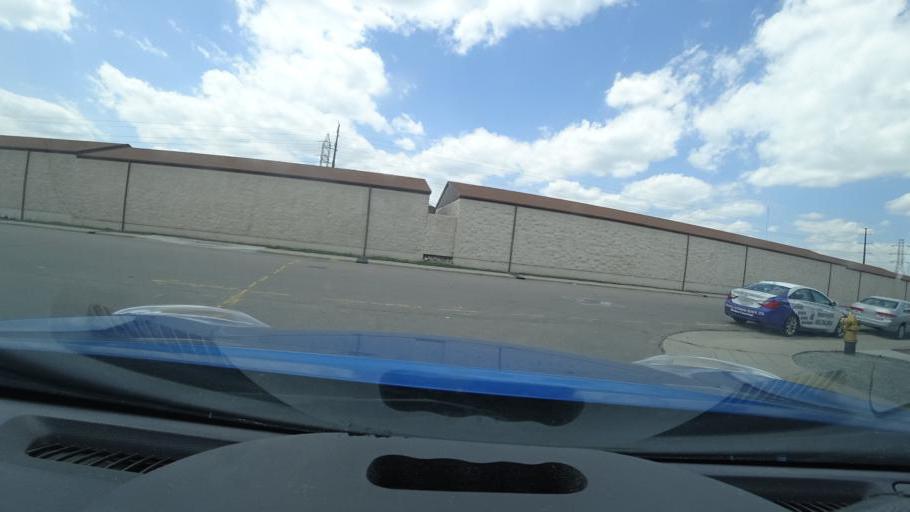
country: US
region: Colorado
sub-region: Arapahoe County
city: Englewood
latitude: 39.6767
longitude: -105.0015
